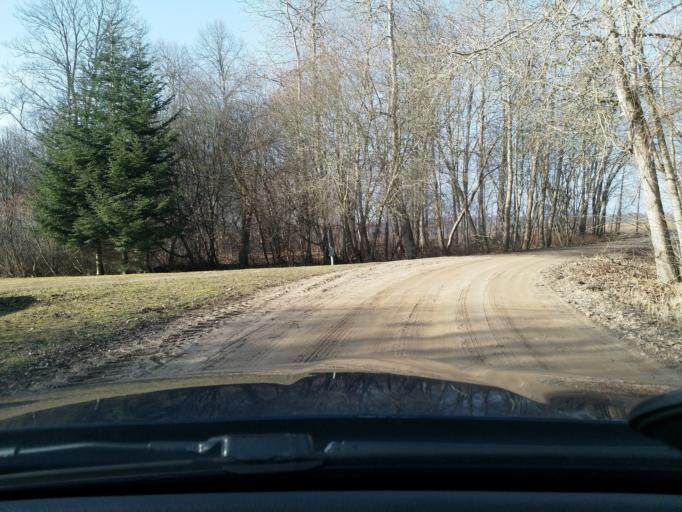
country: LV
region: Kuldigas Rajons
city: Kuldiga
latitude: 56.8712
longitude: 21.9532
